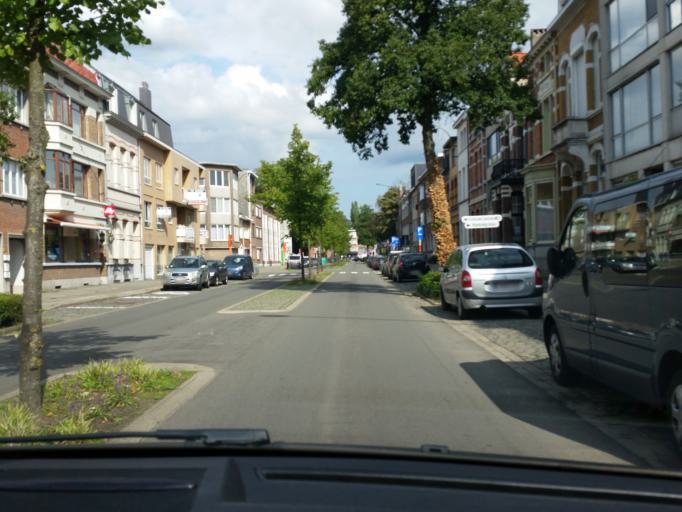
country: BE
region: Flanders
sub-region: Provincie Antwerpen
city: Mortsel
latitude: 51.1686
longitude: 4.4466
